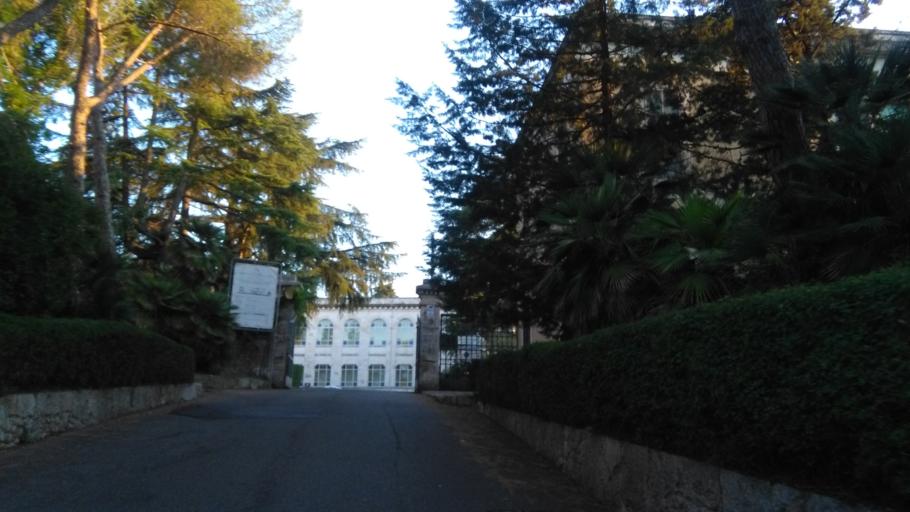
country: IT
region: Apulia
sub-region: Provincia di Bari
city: Putignano
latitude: 40.8239
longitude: 17.1086
